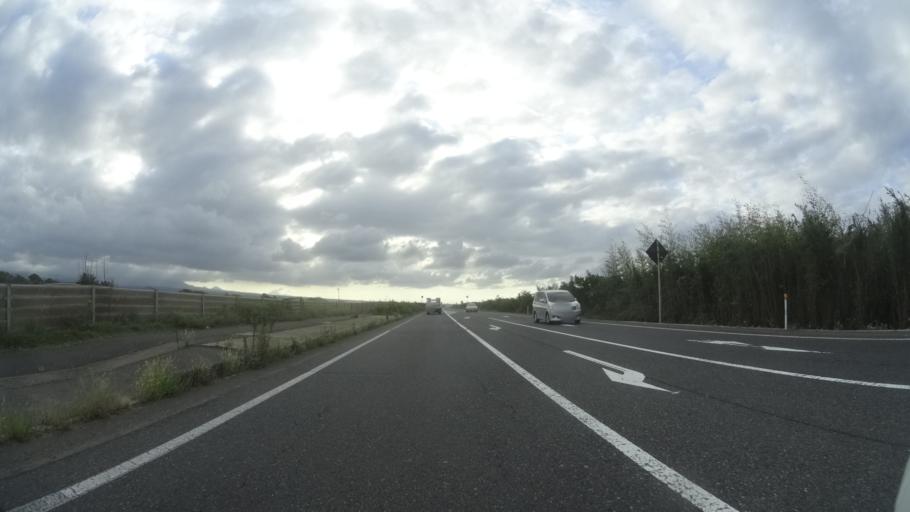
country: JP
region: Tottori
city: Kurayoshi
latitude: 35.5003
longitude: 133.7435
